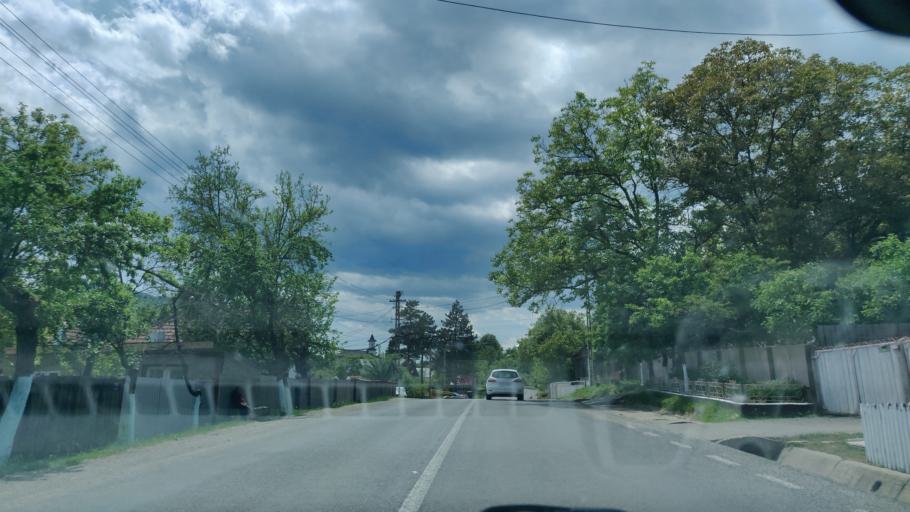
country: RO
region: Vrancea
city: Matacina
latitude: 45.8832
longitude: 26.8072
